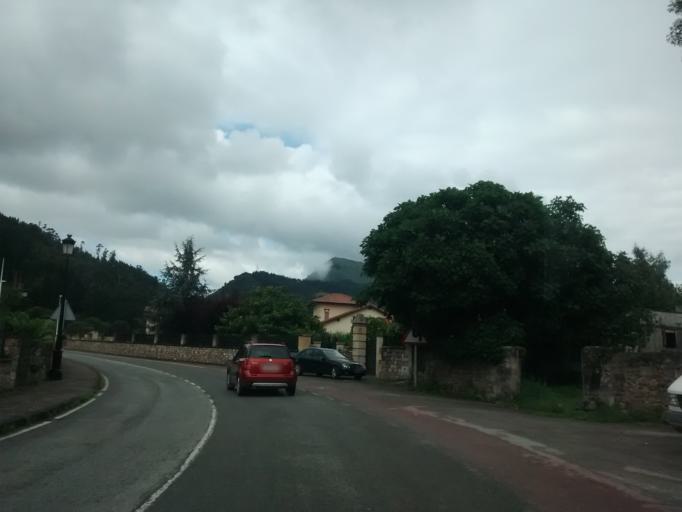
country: ES
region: Cantabria
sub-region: Provincia de Cantabria
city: Luzmela
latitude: 43.2894
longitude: -4.2261
